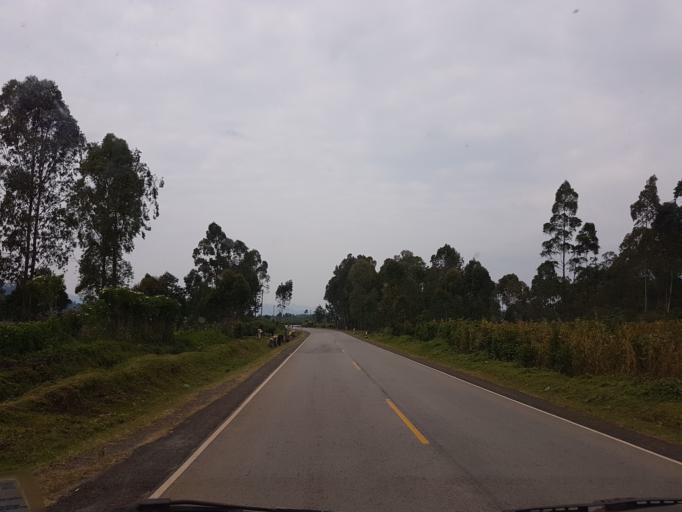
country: UG
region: Western Region
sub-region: Kisoro District
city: Kisoro
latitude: -1.3151
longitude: 29.7241
